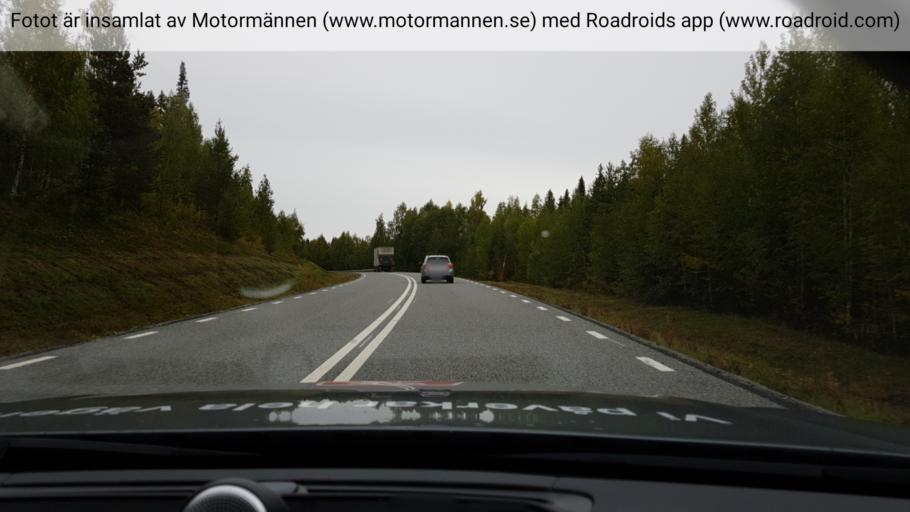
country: SE
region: Jaemtland
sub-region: Stroemsunds Kommun
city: Stroemsund
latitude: 64.0958
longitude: 15.5775
